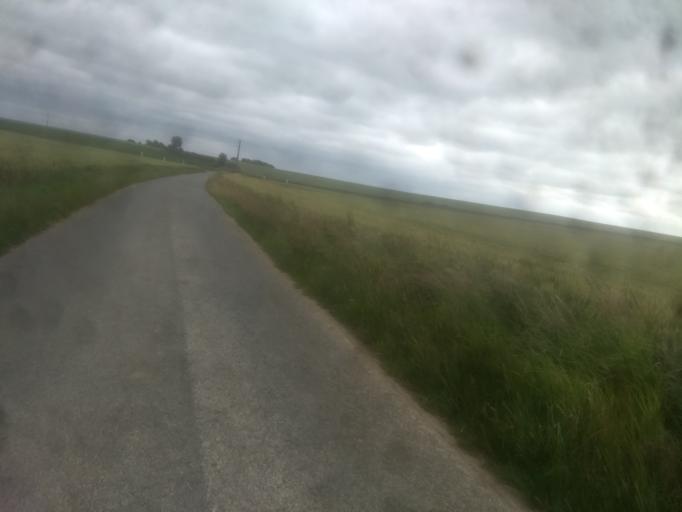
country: FR
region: Nord-Pas-de-Calais
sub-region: Departement du Pas-de-Calais
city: Mont-Saint-Eloi
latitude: 50.3524
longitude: 2.7131
